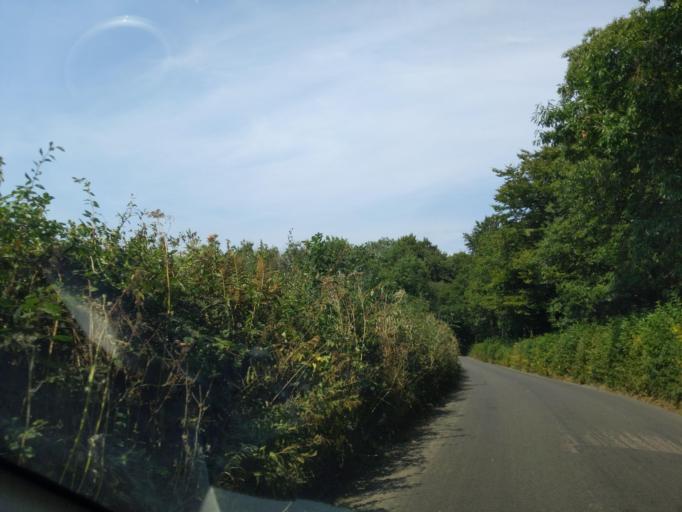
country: GB
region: England
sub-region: Devon
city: Winkleigh
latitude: 50.8785
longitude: -3.8935
